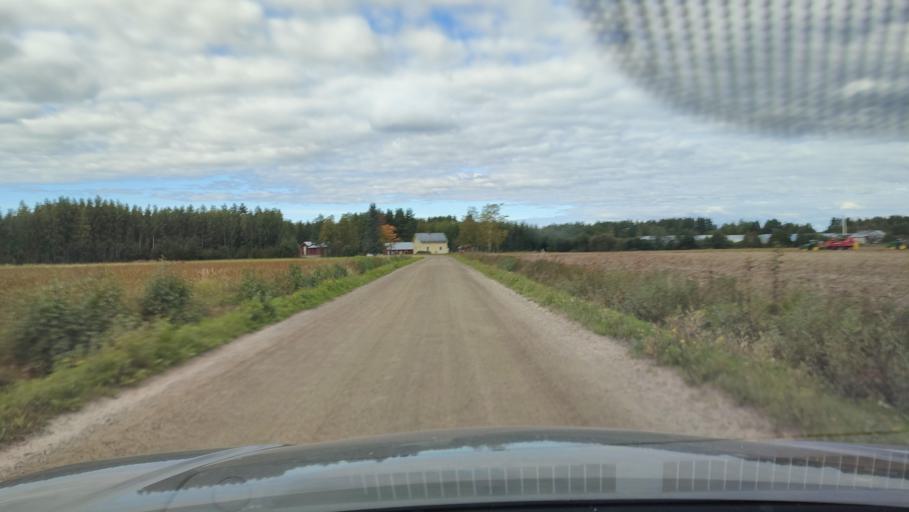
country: FI
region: Southern Ostrobothnia
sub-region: Suupohja
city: Karijoki
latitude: 62.2349
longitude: 21.6040
